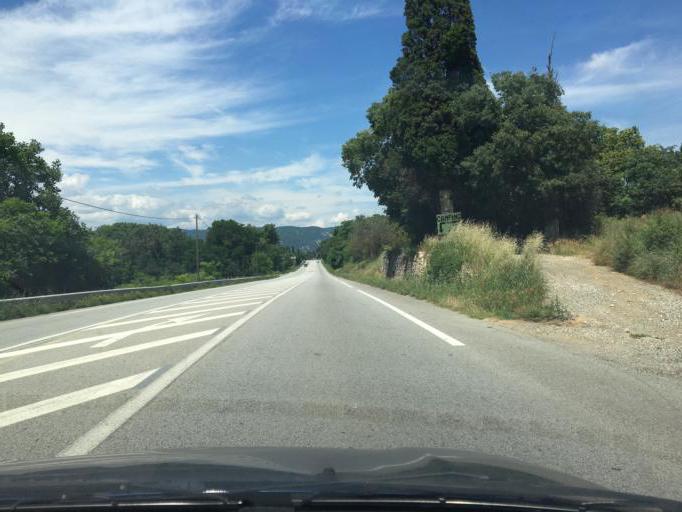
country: FR
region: Rhone-Alpes
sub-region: Departement de la Drome
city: Ancone
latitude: 44.5843
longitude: 4.7525
